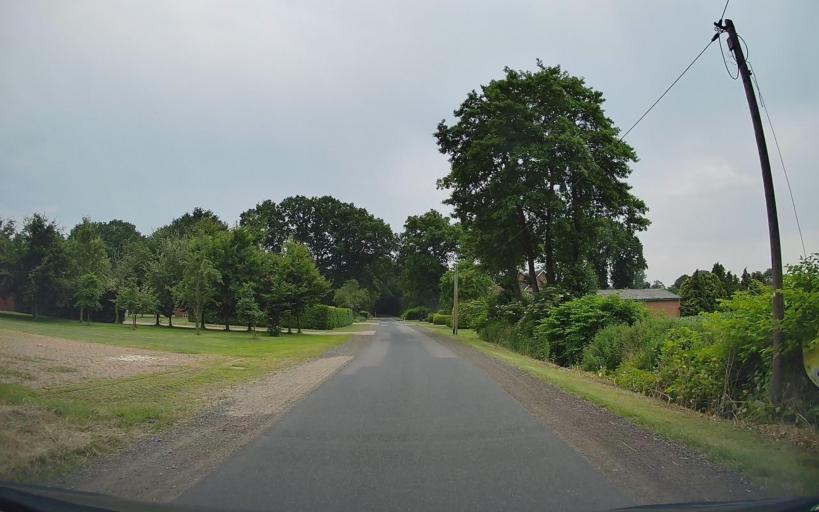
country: DE
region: Lower Saxony
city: Friesoythe
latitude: 53.0286
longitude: 7.9023
